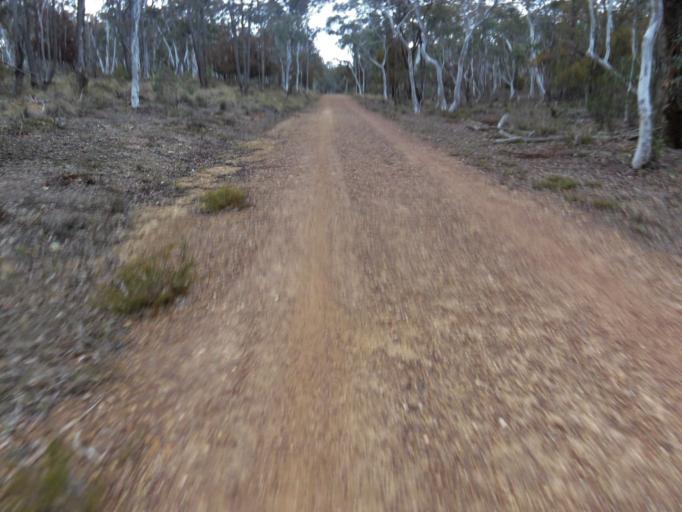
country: AU
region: Australian Capital Territory
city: Acton
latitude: -35.2645
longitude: 149.0958
